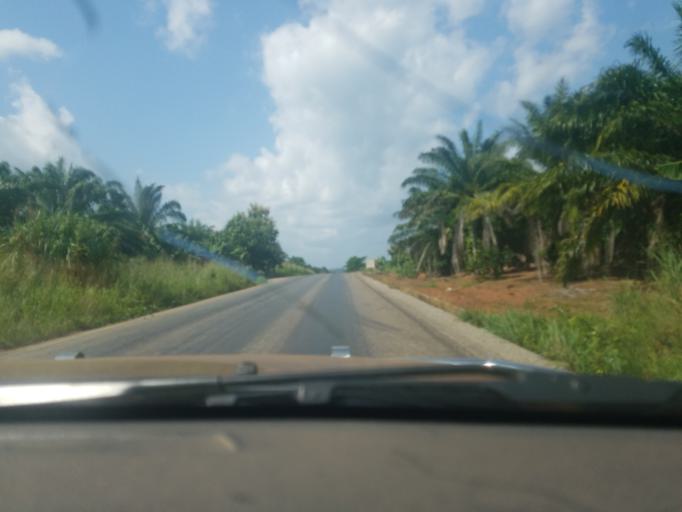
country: GH
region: Western
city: Bibiani
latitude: 6.8756
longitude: -2.4303
